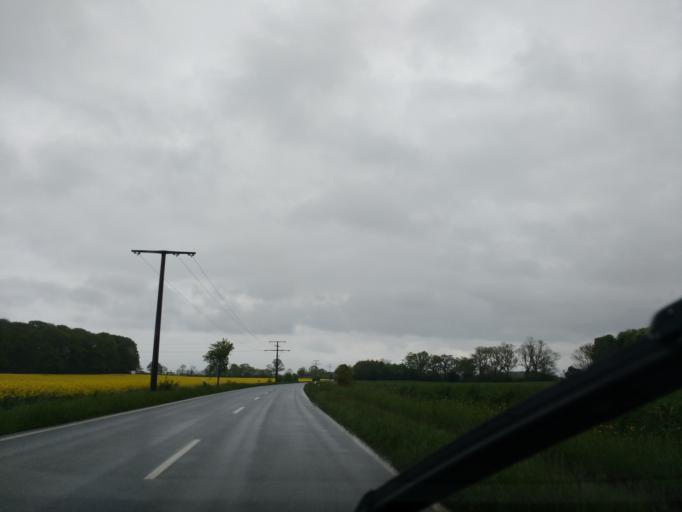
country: DE
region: Schleswig-Holstein
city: Damp
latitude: 54.5797
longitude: 9.9817
